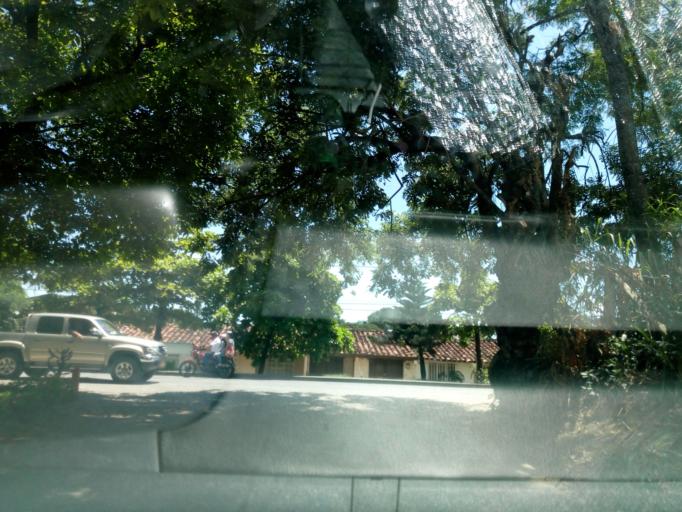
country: CO
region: Valle del Cauca
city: Cartago
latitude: 4.7510
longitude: -75.9266
